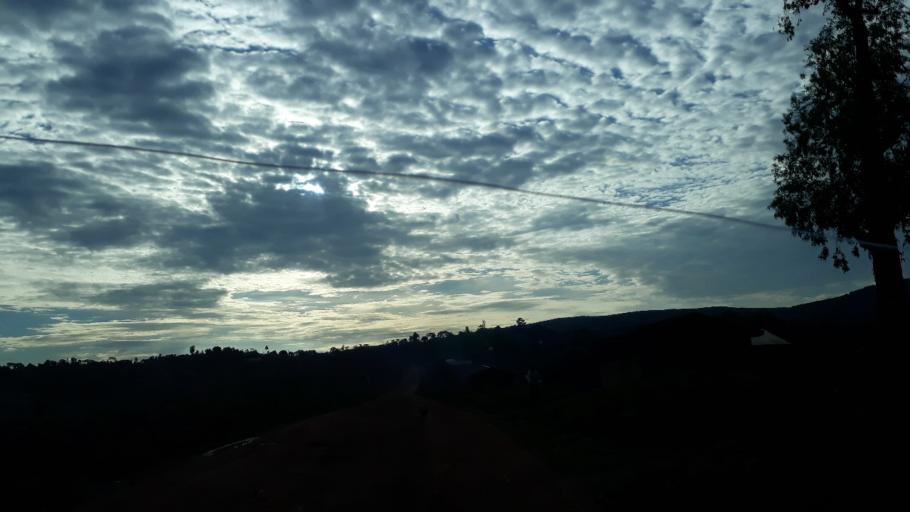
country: UG
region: Northern Region
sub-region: Zombo District
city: Paidha
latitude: 2.2306
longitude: 30.8387
